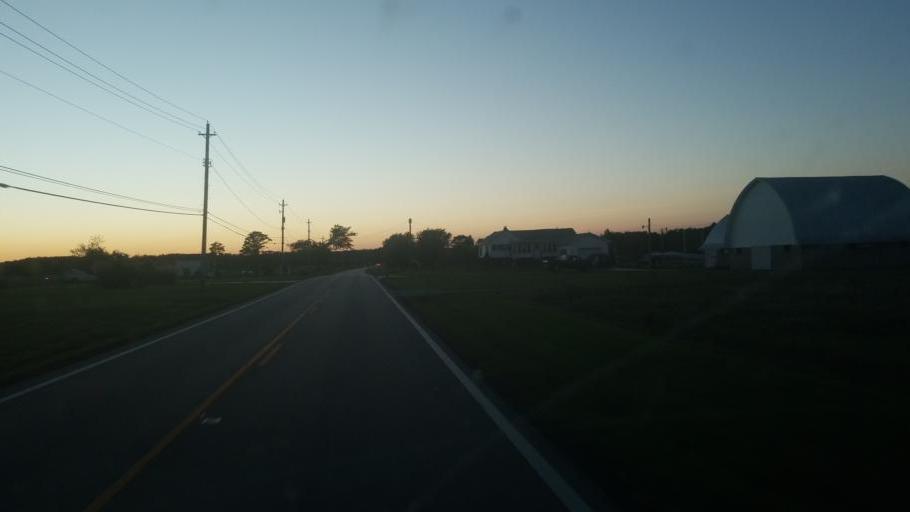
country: US
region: Ohio
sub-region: Ashtabula County
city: Andover
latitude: 41.7518
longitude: -80.6060
